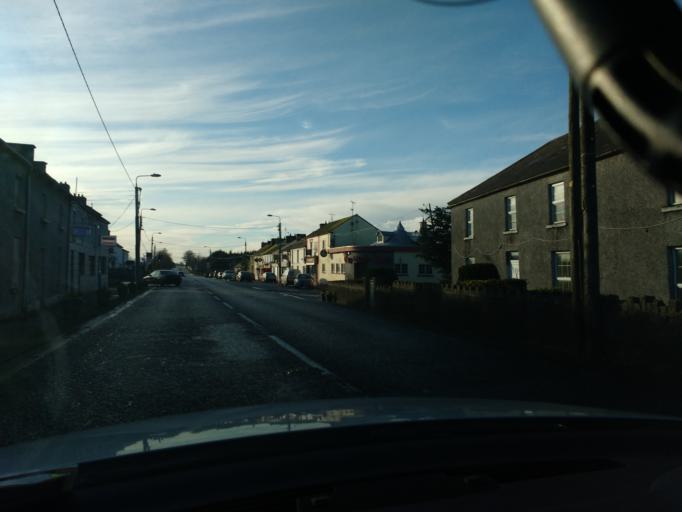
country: IE
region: Munster
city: Thurles
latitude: 52.6395
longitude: -7.7380
